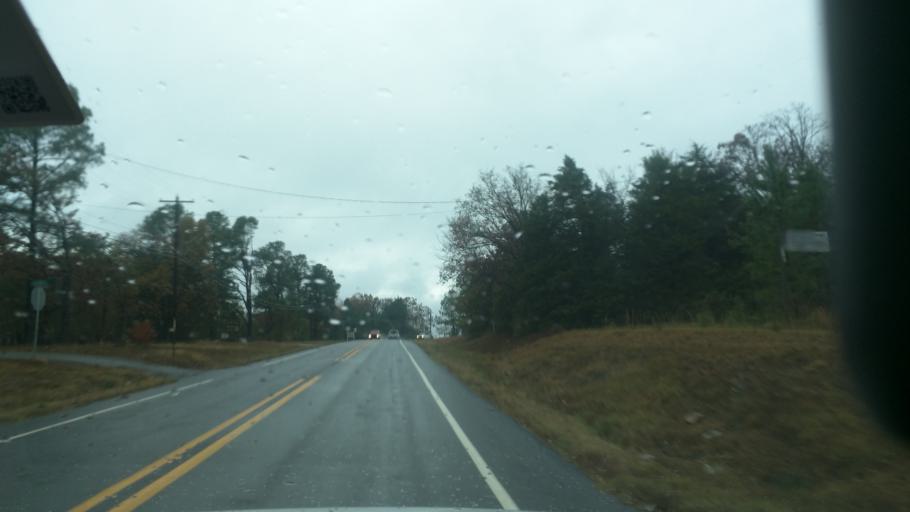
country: US
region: Arkansas
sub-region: Franklin County
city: Ozark
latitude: 35.5019
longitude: -93.8445
